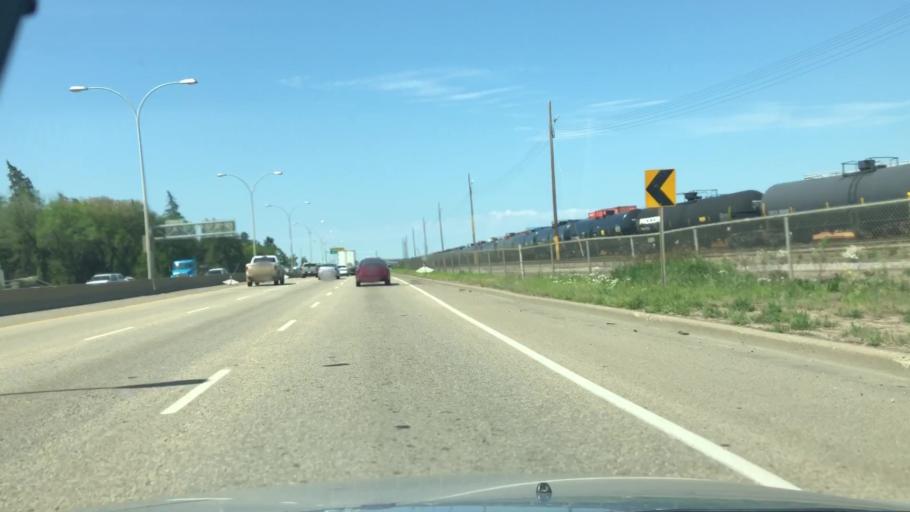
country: CA
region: Alberta
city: Edmonton
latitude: 53.5816
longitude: -113.4994
